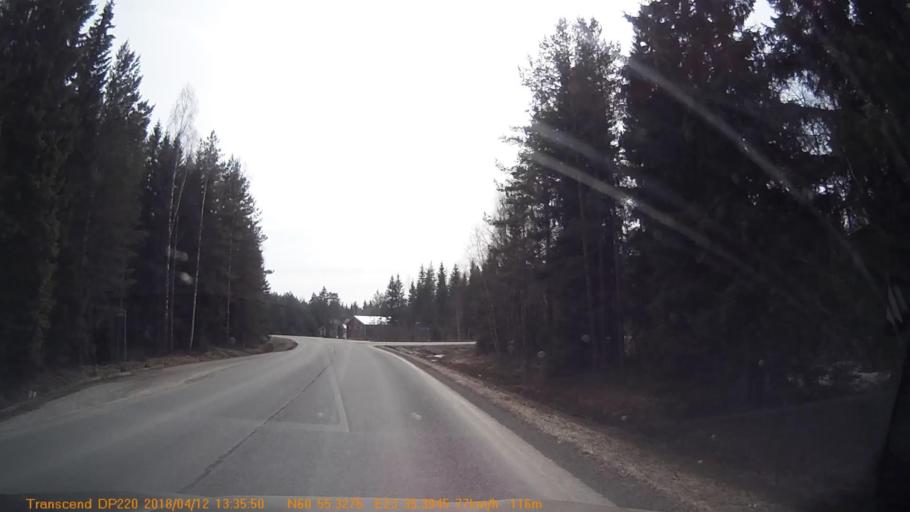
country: FI
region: Haeme
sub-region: Forssa
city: Forssa
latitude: 60.9219
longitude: 23.5898
